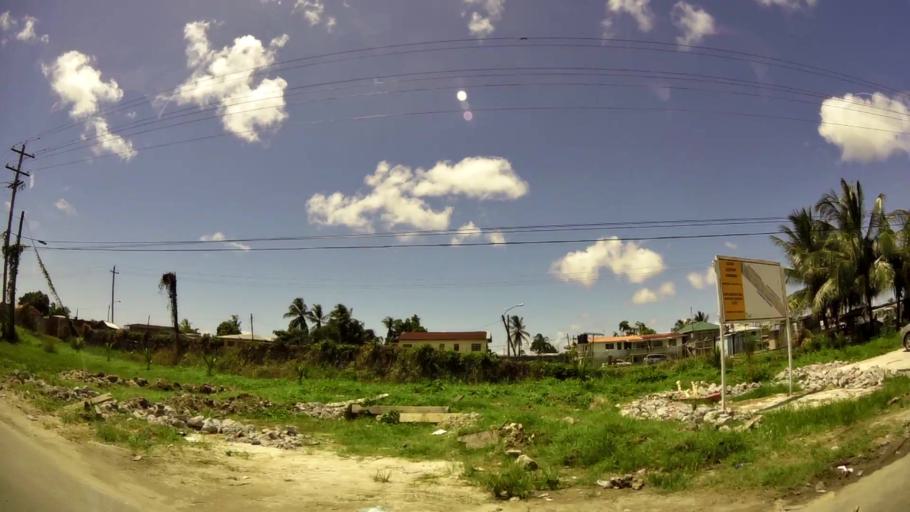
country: GY
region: Demerara-Mahaica
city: Georgetown
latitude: 6.7882
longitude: -58.1478
